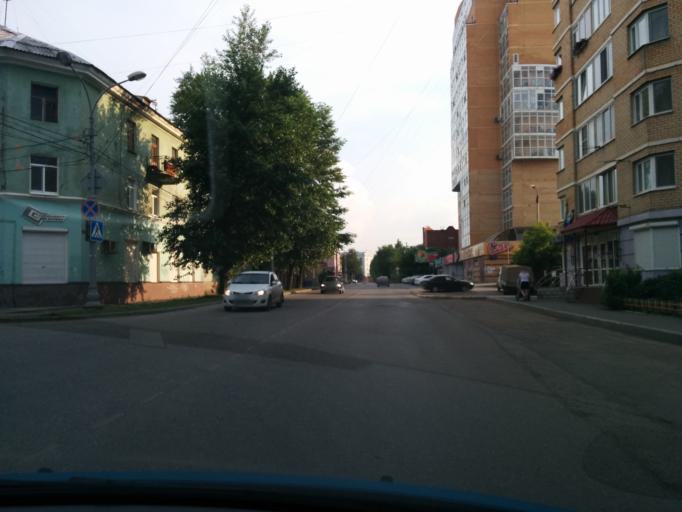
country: RU
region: Perm
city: Perm
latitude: 58.0224
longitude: 56.2905
